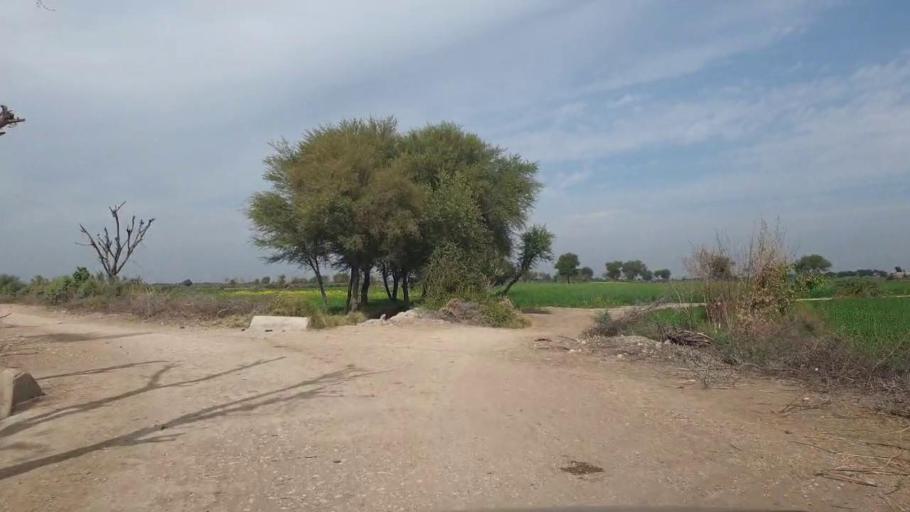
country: PK
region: Sindh
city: Sanghar
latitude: 26.0469
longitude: 68.9062
